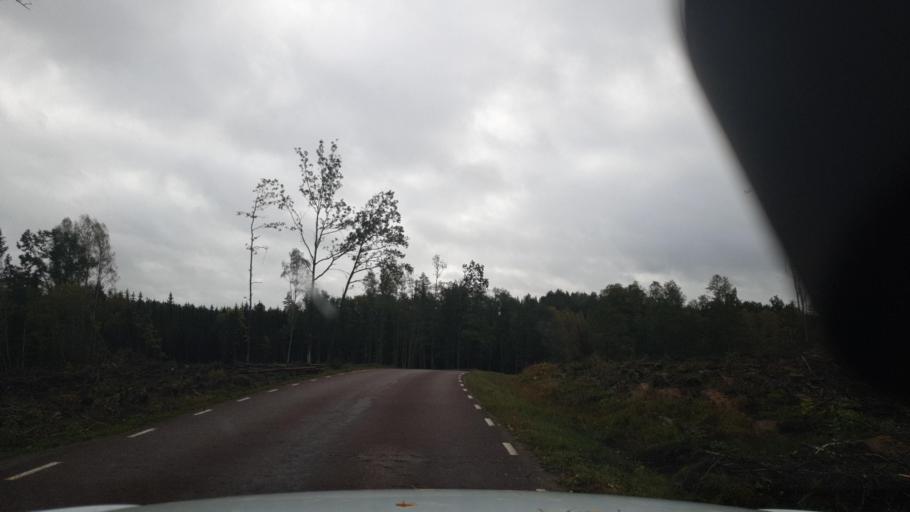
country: SE
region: Vaermland
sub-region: Grums Kommun
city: Grums
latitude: 59.4287
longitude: 13.0854
